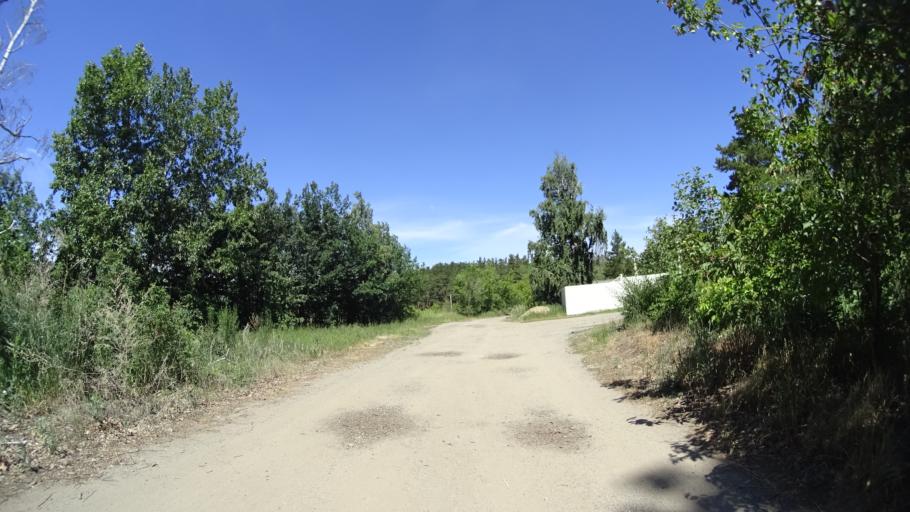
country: RU
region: Chelyabinsk
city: Troitsk
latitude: 54.0503
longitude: 61.6271
